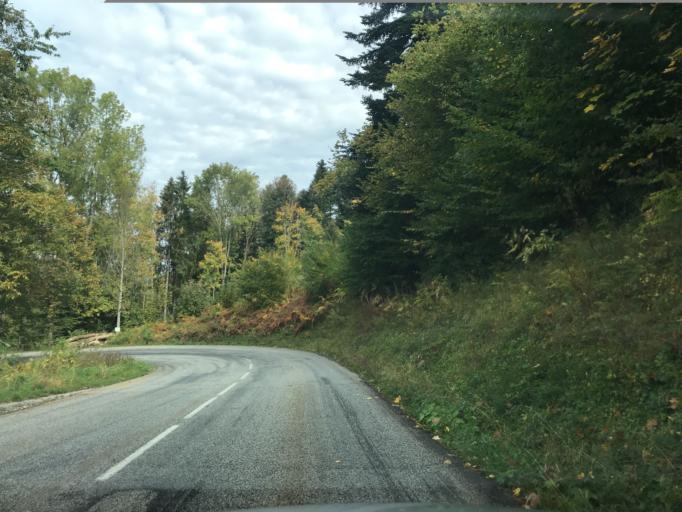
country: FR
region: Rhone-Alpes
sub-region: Departement de la Savoie
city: Les Echelles
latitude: 45.4642
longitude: 5.8271
